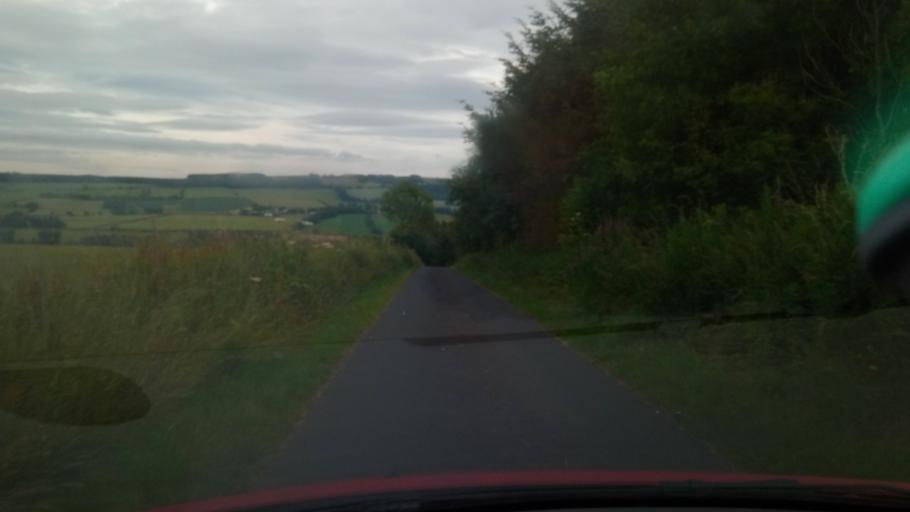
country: GB
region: Scotland
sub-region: The Scottish Borders
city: Saint Boswells
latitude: 55.5027
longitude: -2.6240
